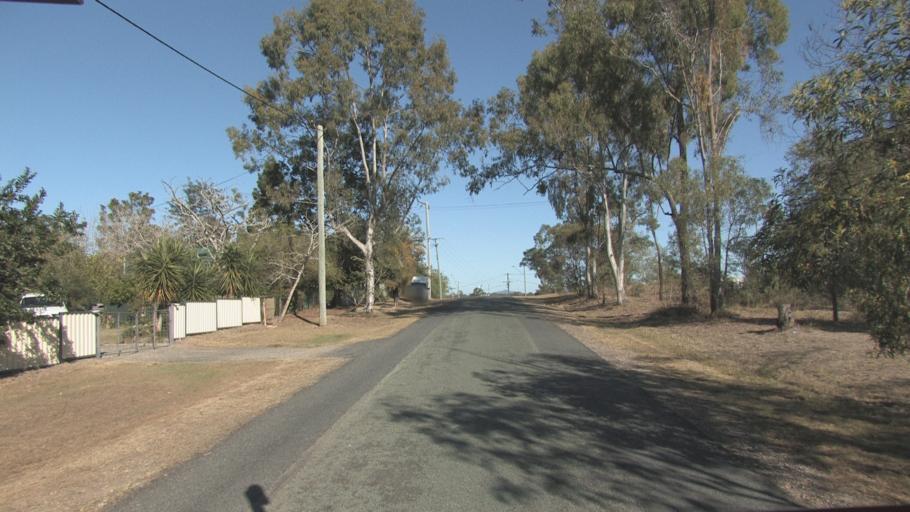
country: AU
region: Queensland
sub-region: Logan
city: Cedar Vale
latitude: -27.8316
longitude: 153.0293
